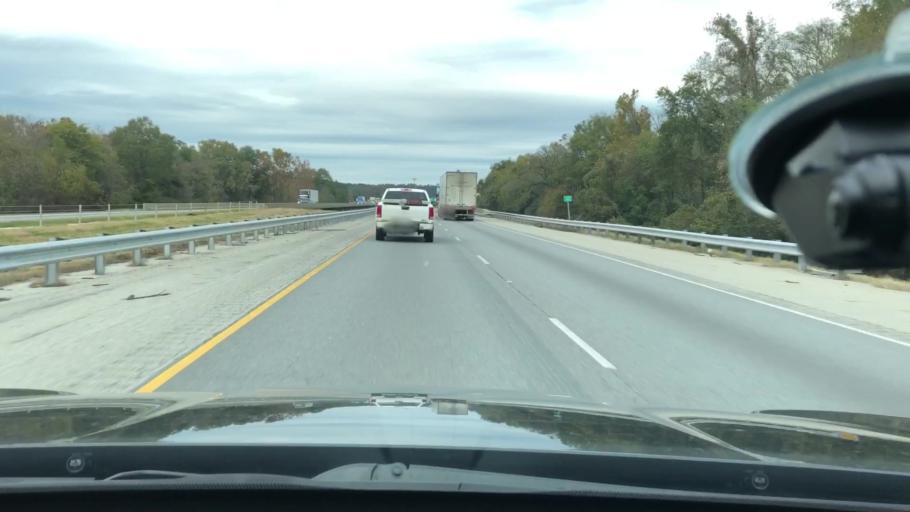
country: US
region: Arkansas
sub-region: Clark County
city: Arkadelphia
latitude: 34.1737
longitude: -93.0744
